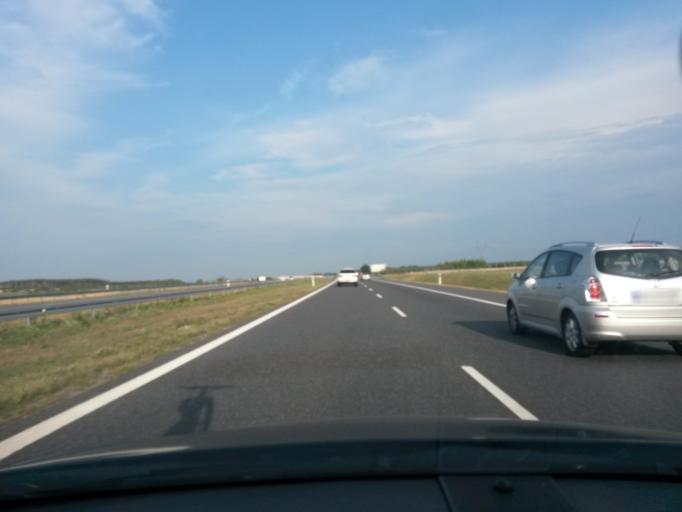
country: PL
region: Lodz Voivodeship
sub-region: Powiat zgierski
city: Ozorkow
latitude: 51.9302
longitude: 19.2893
